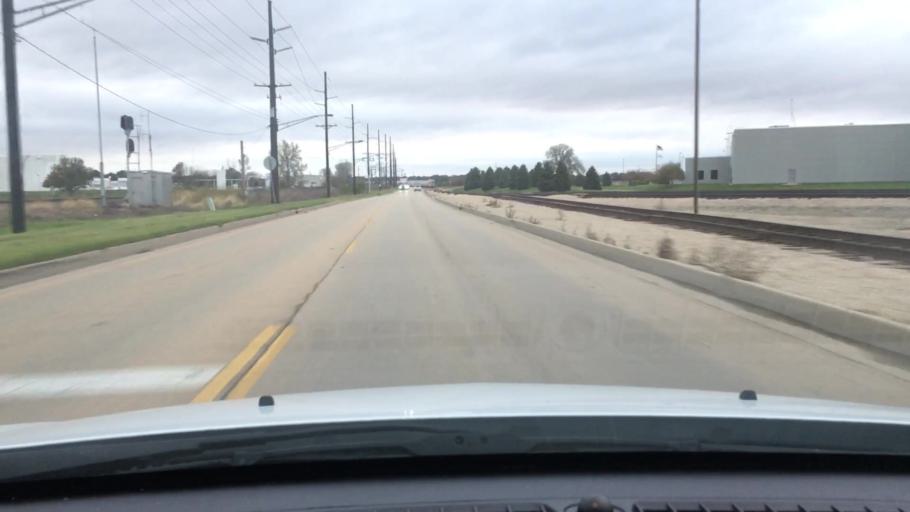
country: US
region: Illinois
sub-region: Ogle County
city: Rochelle
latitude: 41.9101
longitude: -89.0478
